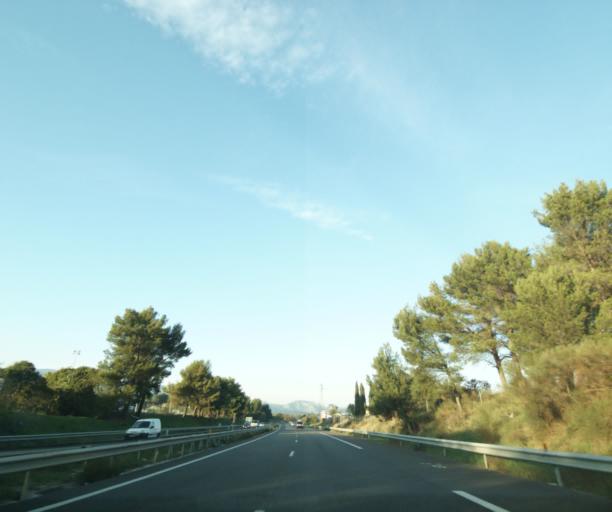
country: FR
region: Provence-Alpes-Cote d'Azur
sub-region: Departement des Bouches-du-Rhone
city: Aubagne
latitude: 43.2871
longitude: 5.5864
